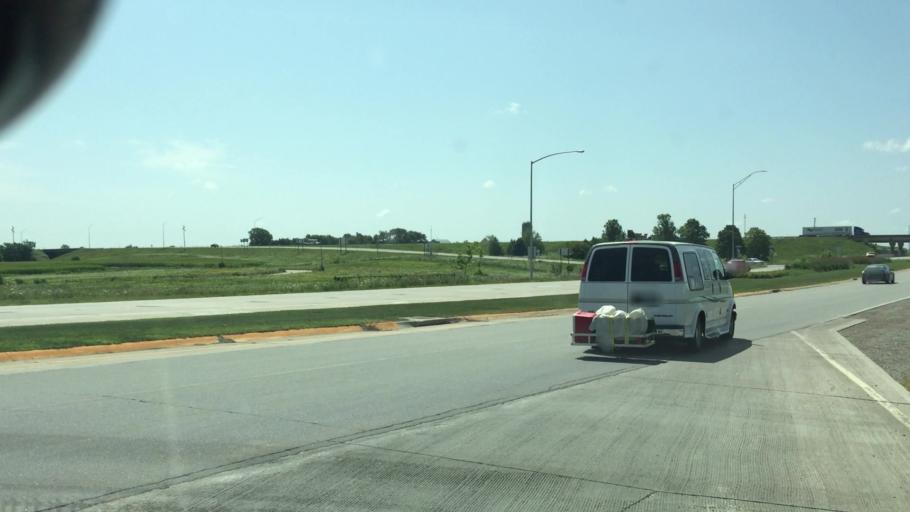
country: US
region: Iowa
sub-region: Poweshiek County
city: Grinnell
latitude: 41.6996
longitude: -92.7273
